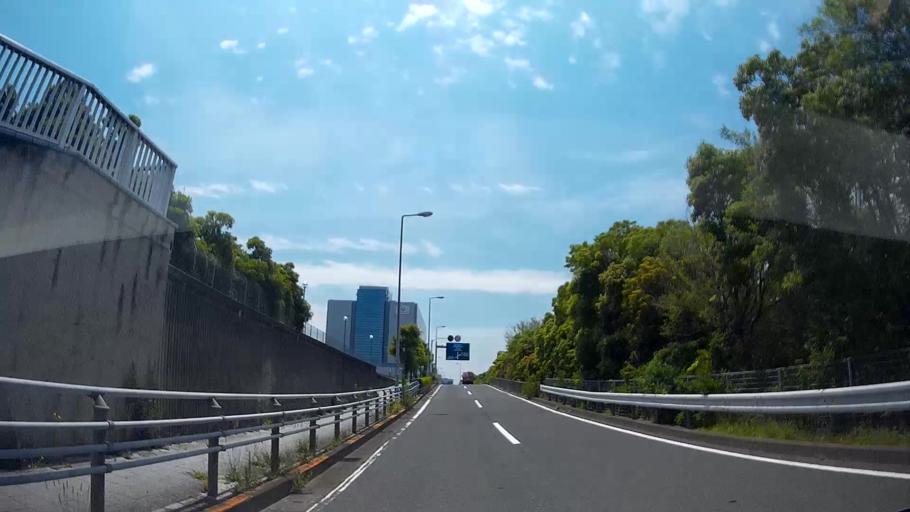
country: JP
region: Kanagawa
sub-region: Kawasaki-shi
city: Kawasaki
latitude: 35.5437
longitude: 139.7915
